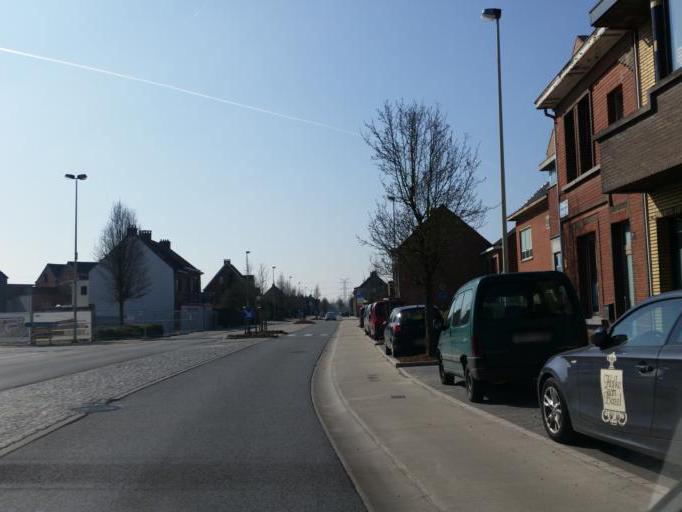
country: BE
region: Flanders
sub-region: Provincie Oost-Vlaanderen
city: Kruibeke
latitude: 51.1439
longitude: 4.2966
